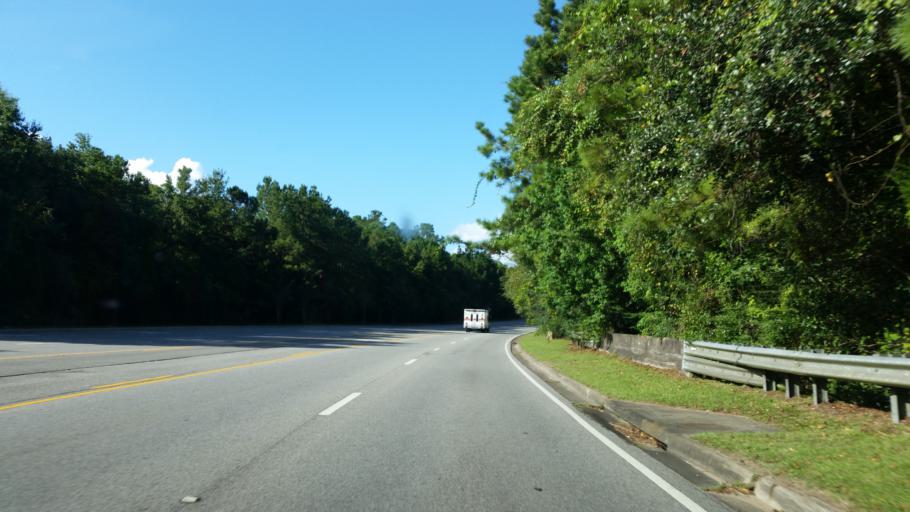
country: US
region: Alabama
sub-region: Mobile County
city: Prichard
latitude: 30.7064
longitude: -88.1740
